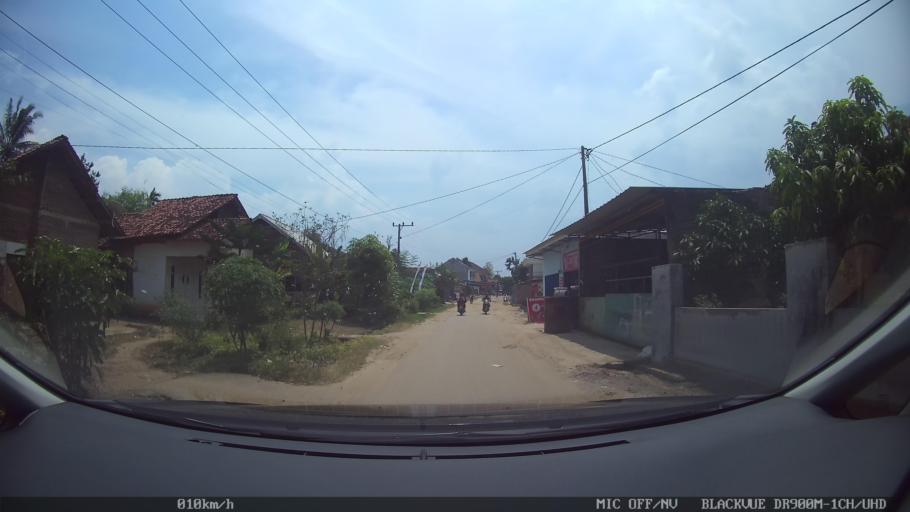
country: ID
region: Lampung
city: Natar
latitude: -5.3144
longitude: 105.2105
